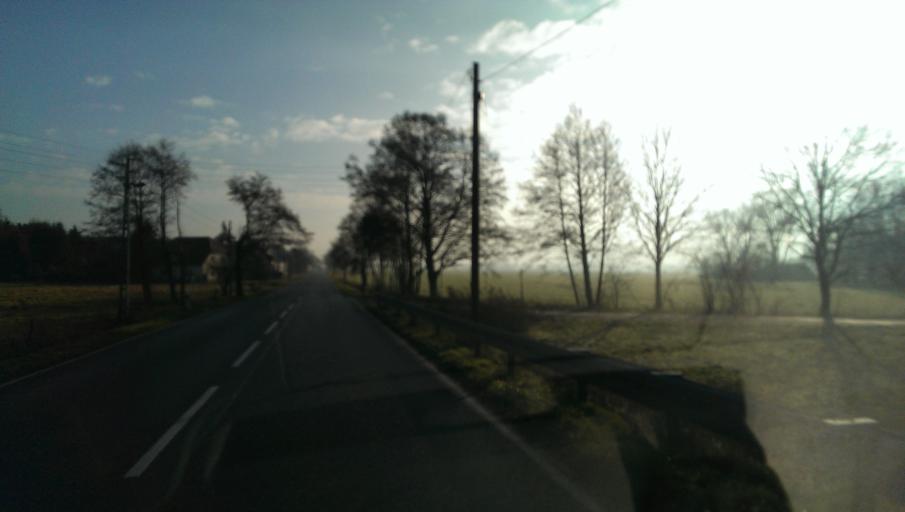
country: DE
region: Brandenburg
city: Schilda
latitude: 51.6263
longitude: 13.3223
